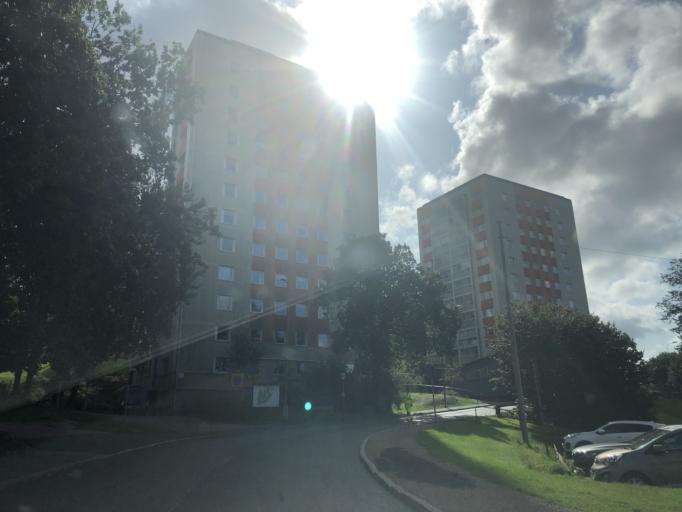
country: SE
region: Vaestra Goetaland
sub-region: Goteborg
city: Majorna
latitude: 57.7191
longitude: 11.9342
